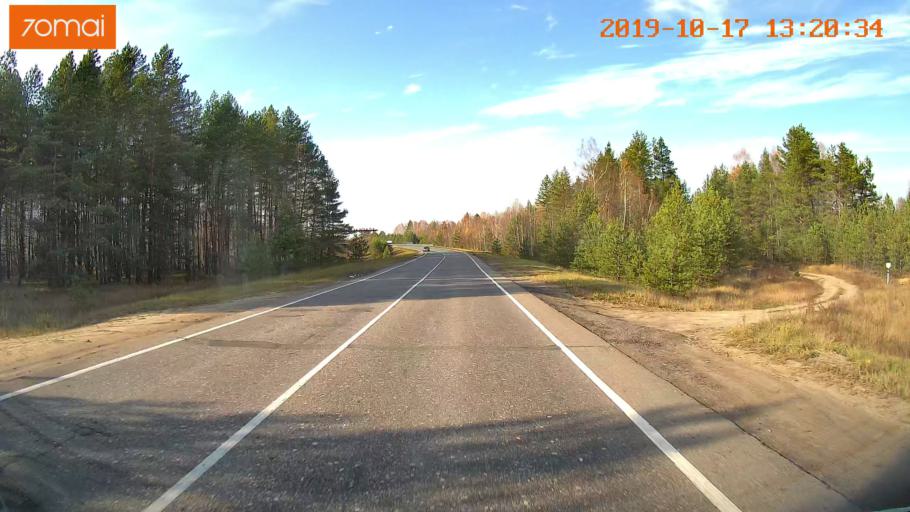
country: RU
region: Rjazan
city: Gus'-Zheleznyy
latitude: 55.0770
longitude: 41.0476
